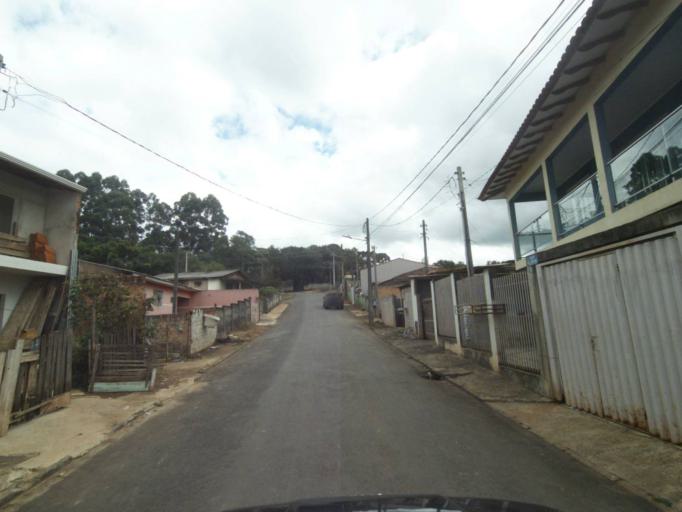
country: BR
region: Parana
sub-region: Telemaco Borba
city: Telemaco Borba
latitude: -24.3179
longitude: -50.6455
